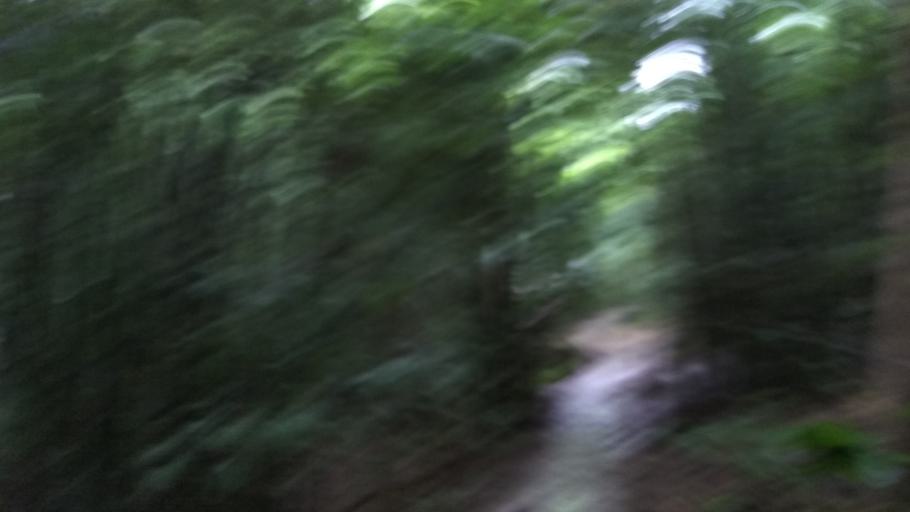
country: IN
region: Tripura
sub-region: Dhalai
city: Kamalpur
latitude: 24.1695
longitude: 91.9002
